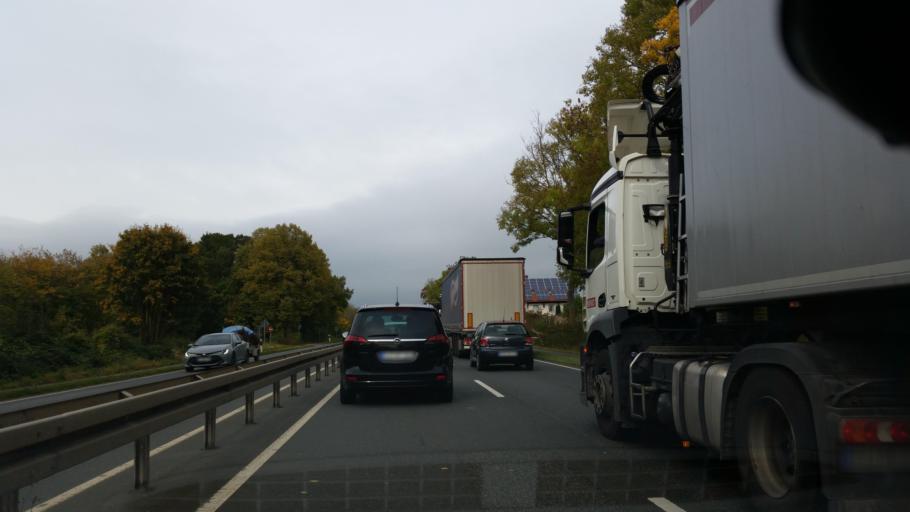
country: DE
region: Lower Saxony
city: Giesen
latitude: 52.1891
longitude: 9.9247
